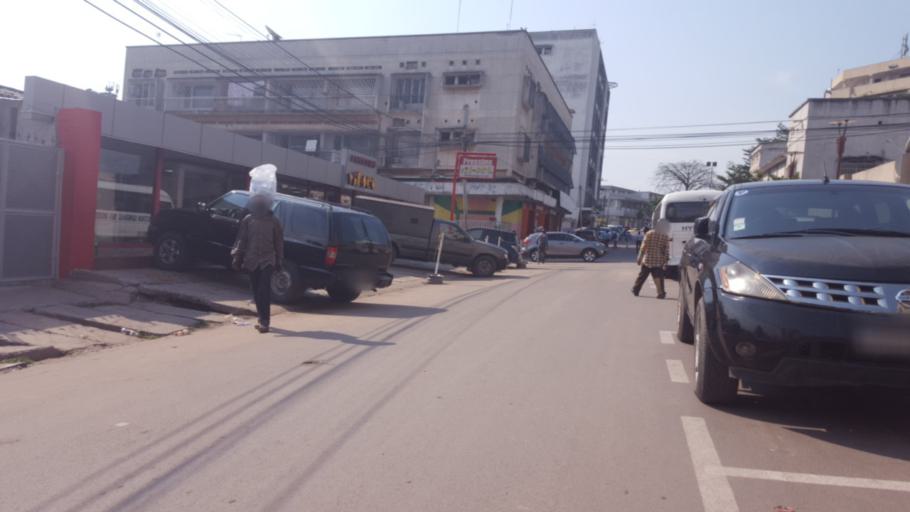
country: CD
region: Kinshasa
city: Kinshasa
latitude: -4.3060
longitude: 15.3058
